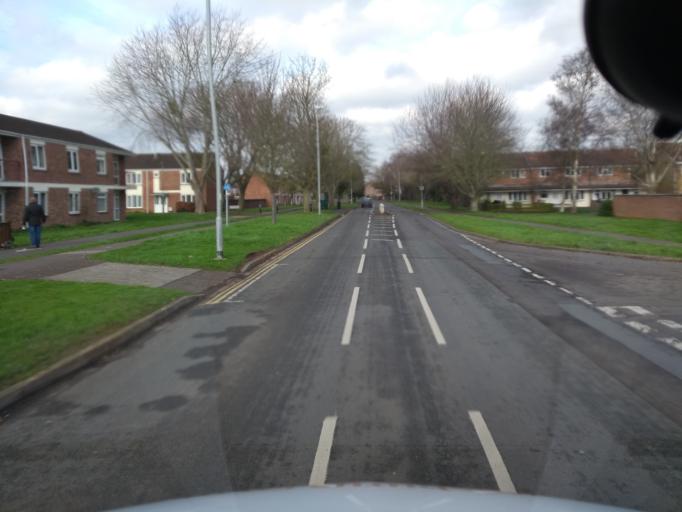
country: GB
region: England
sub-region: Somerset
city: Taunton
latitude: 51.0107
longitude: -3.0754
